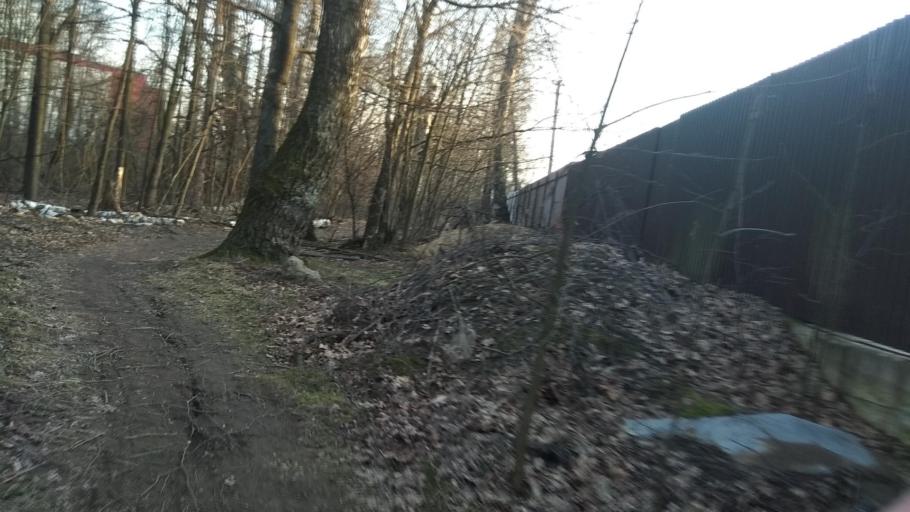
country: RU
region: Moskovskaya
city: Razvilka
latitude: 55.5678
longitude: 37.7429
